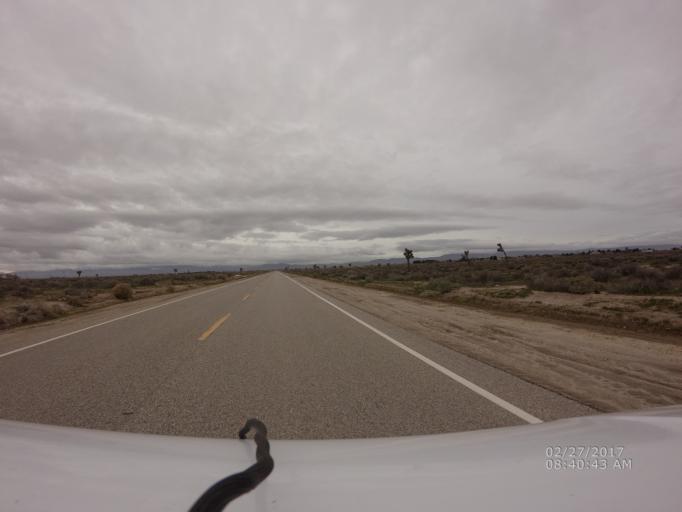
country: US
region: California
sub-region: Los Angeles County
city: Lancaster
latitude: 34.7232
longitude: -118.0592
